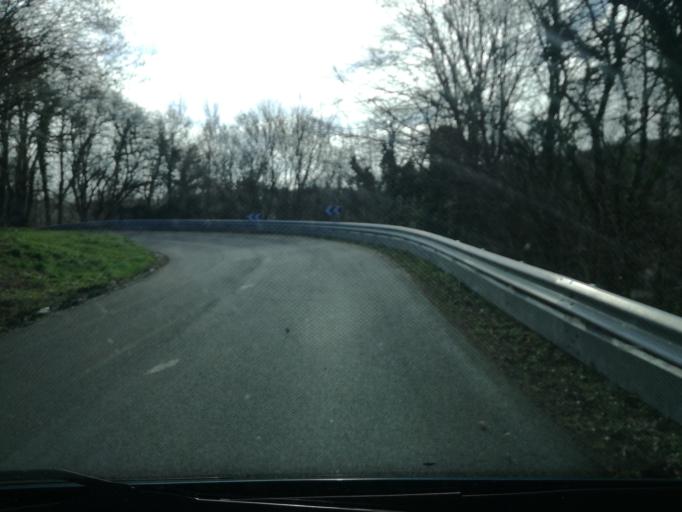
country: FR
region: Haute-Normandie
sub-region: Departement de la Seine-Maritime
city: Yport
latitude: 49.7326
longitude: 0.3238
